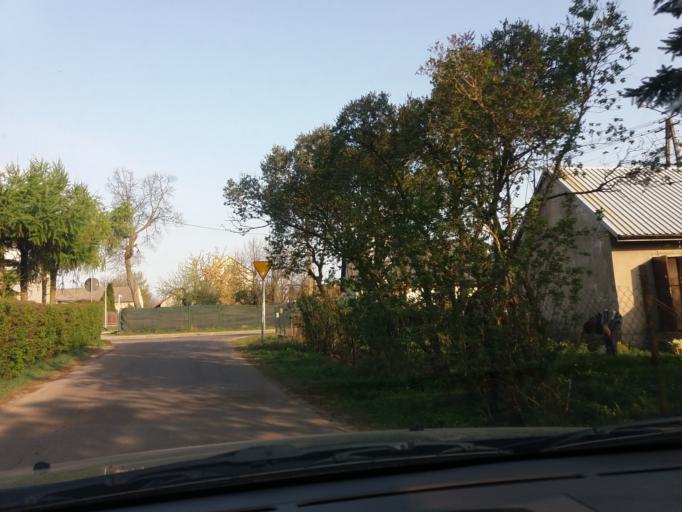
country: PL
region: Masovian Voivodeship
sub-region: Powiat mlawski
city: Mlawa
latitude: 53.1251
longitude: 20.3459
